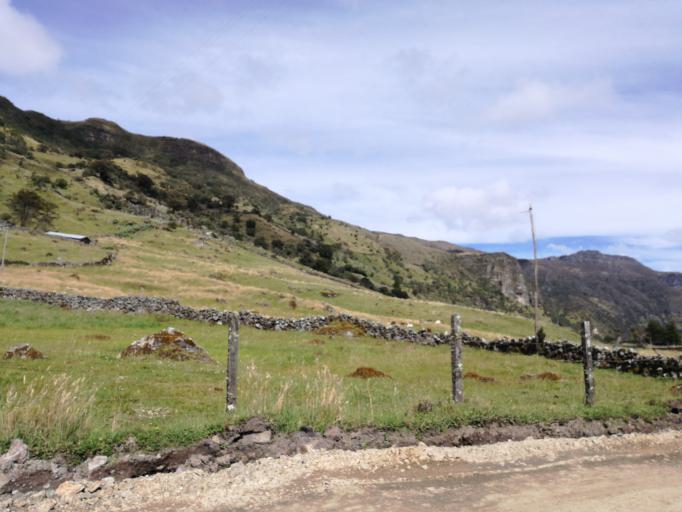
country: CO
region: Boyaca
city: Socha Viejo
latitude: 5.9083
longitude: -72.6823
